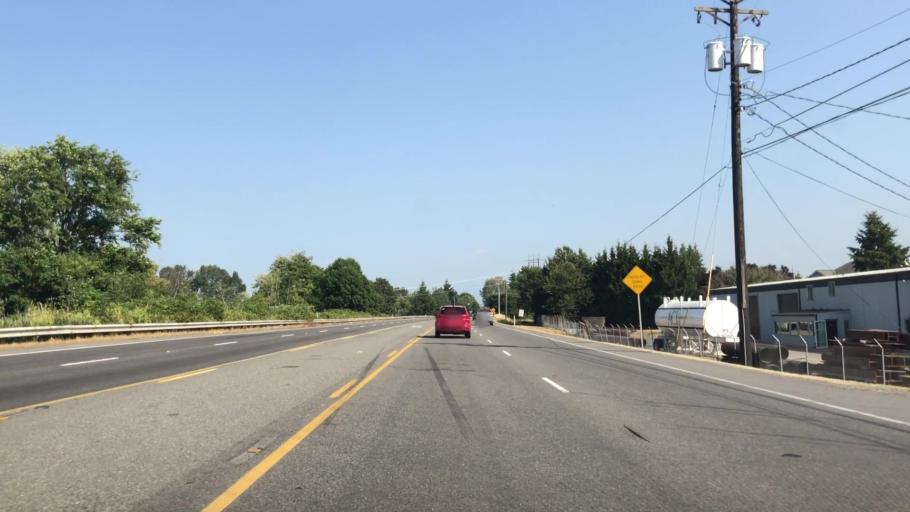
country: US
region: Washington
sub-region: Pierce County
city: Fife
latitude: 47.2234
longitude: -122.3605
